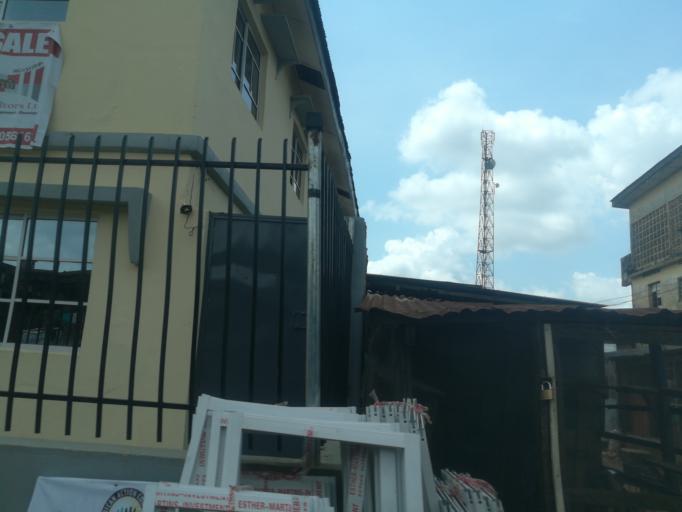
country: NG
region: Oyo
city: Ibadan
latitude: 7.3626
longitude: 3.8785
